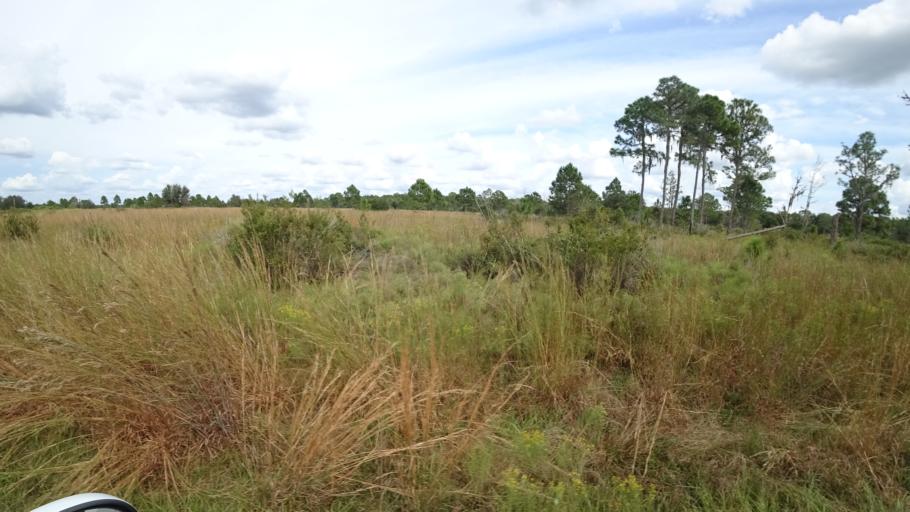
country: US
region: Florida
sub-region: Hillsborough County
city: Wimauma
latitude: 27.5494
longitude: -82.1354
